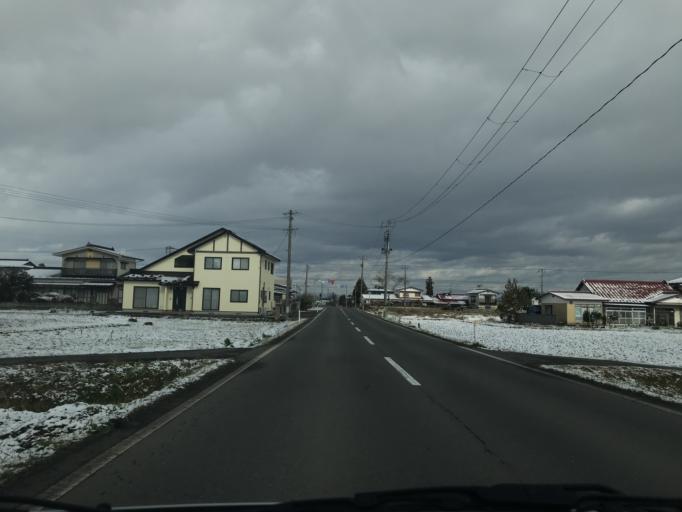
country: JP
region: Iwate
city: Mizusawa
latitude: 39.1614
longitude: 141.1115
